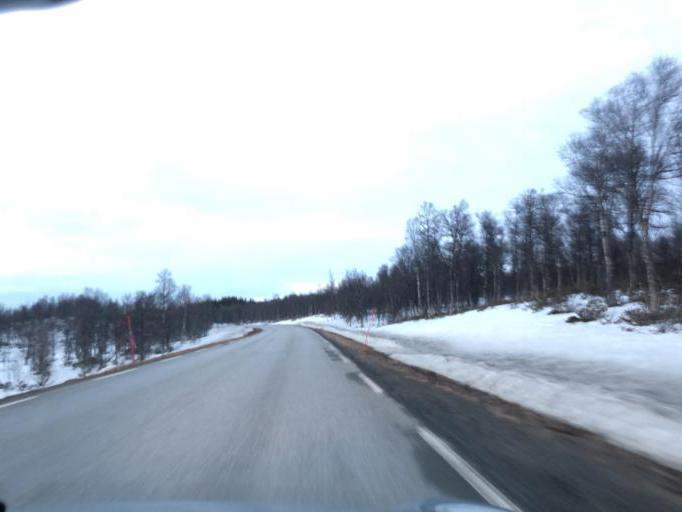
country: NO
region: Sor-Trondelag
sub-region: Tydal
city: Aas
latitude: 62.7145
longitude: 11.8156
